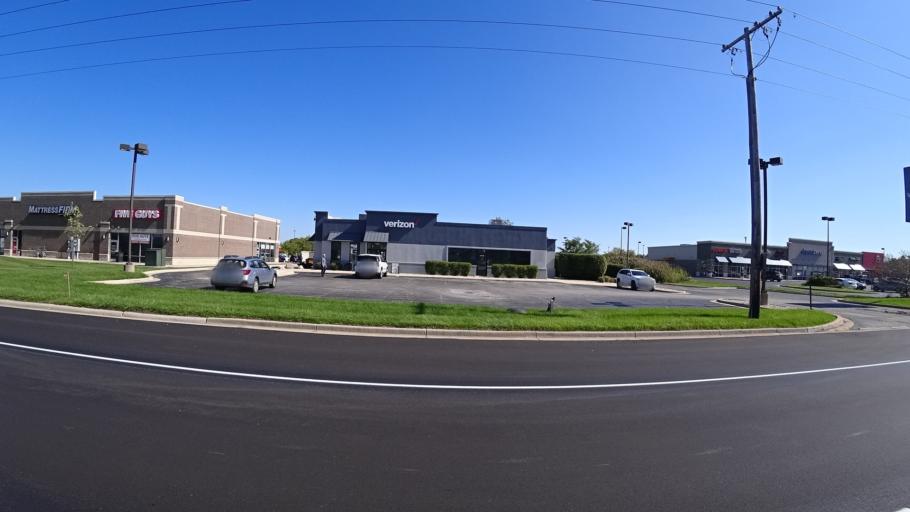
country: US
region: Indiana
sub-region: LaPorte County
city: Michigan City
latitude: 41.6729
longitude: -86.8939
